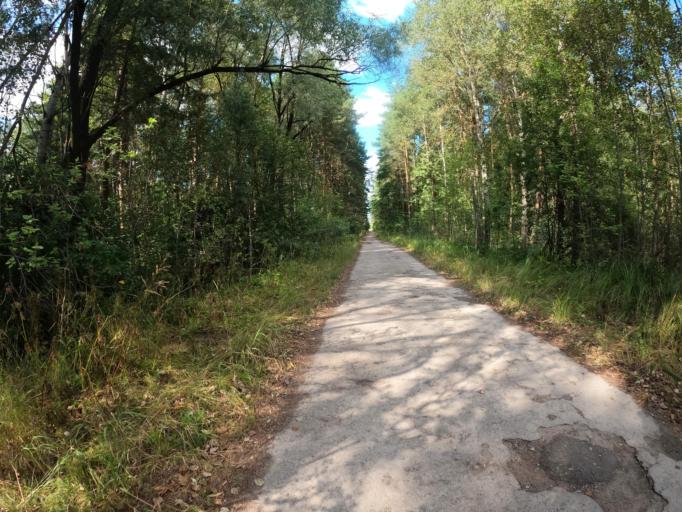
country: RU
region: Moskovskaya
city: Lopatinskiy
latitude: 55.3839
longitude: 38.7078
